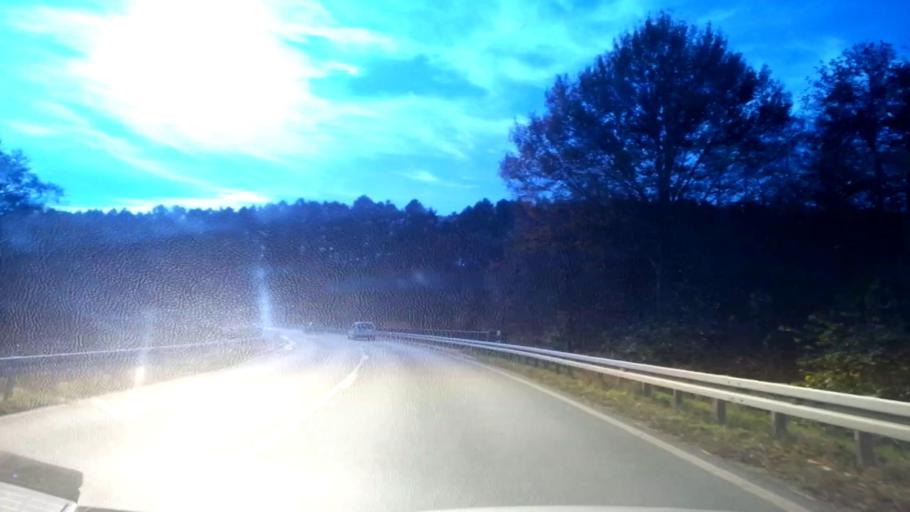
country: DE
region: Bavaria
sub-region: Upper Franconia
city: Seybothenreuth
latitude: 49.9385
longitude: 11.7385
